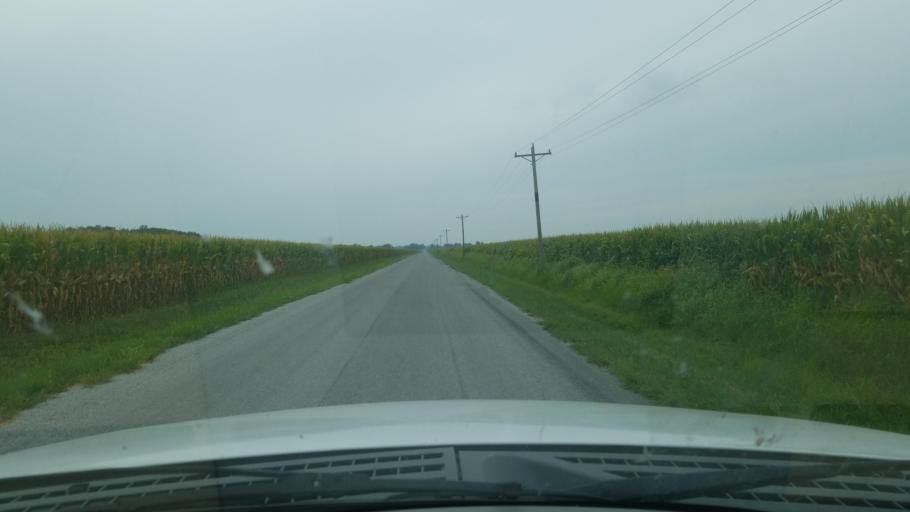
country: US
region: Illinois
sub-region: Saline County
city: Eldorado
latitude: 37.8670
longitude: -88.4634
